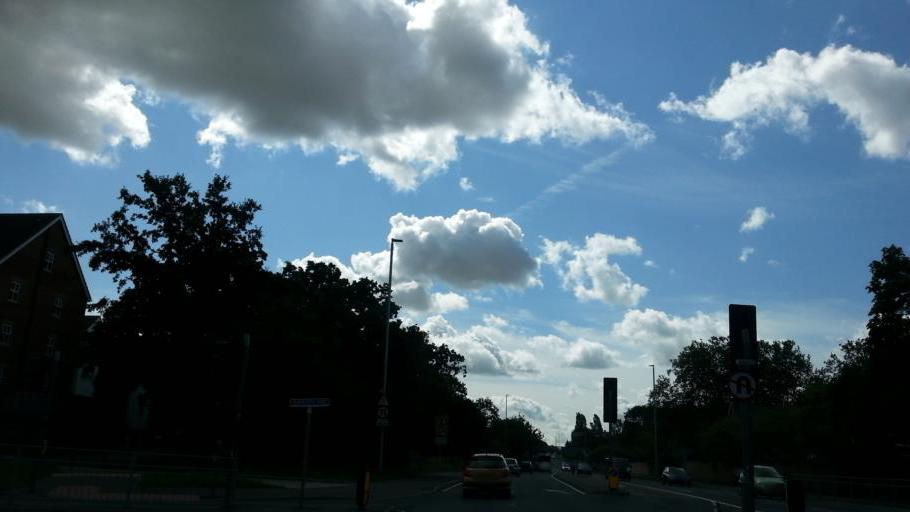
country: GB
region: England
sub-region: Essex
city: Basildon
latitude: 51.5682
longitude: 0.4520
